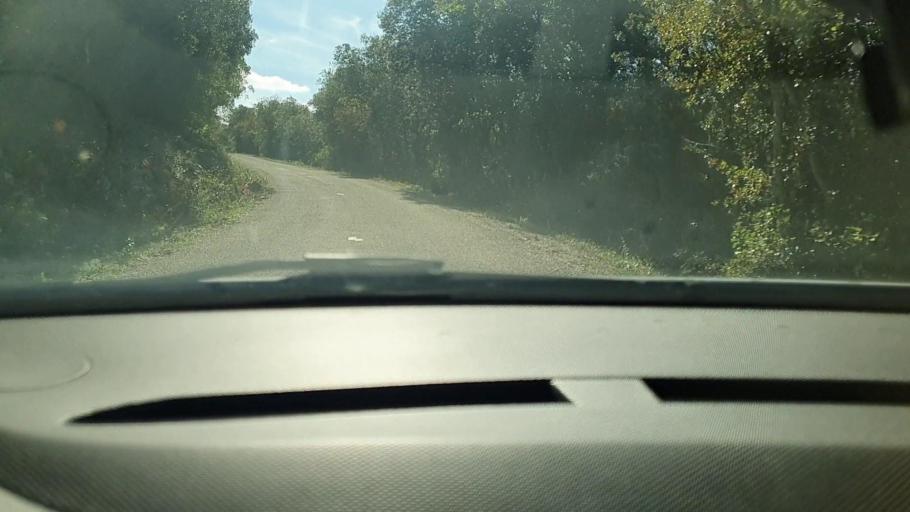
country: FR
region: Languedoc-Roussillon
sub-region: Departement du Gard
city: Barjac
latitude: 44.1995
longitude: 4.3125
